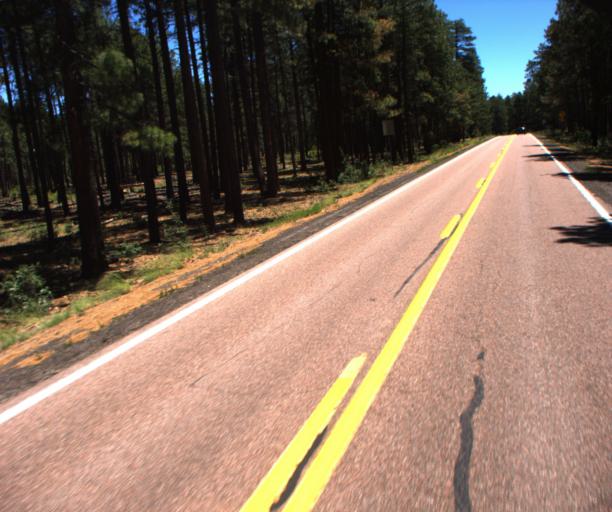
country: US
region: Arizona
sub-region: Gila County
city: Pine
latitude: 34.4511
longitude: -111.4234
